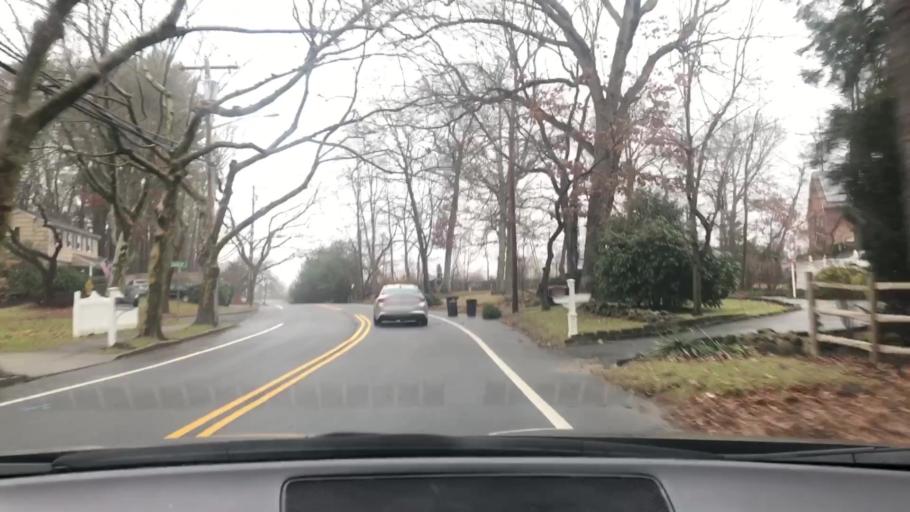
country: US
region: New York
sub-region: Suffolk County
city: South Huntington
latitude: 40.8325
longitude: -73.3851
